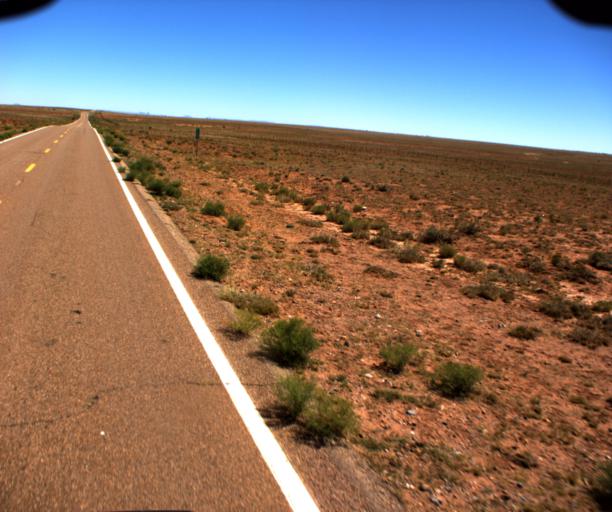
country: US
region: Arizona
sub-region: Navajo County
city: Winslow
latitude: 34.8419
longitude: -110.6699
